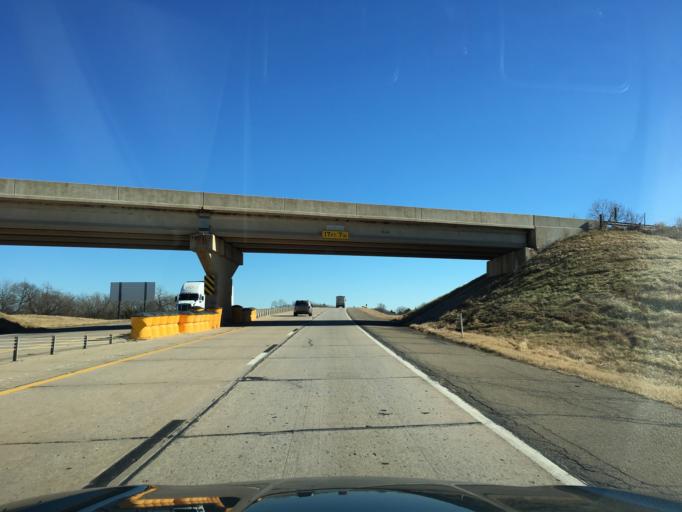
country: US
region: Oklahoma
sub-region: Pawnee County
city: Pawnee
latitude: 36.2378
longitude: -96.9267
